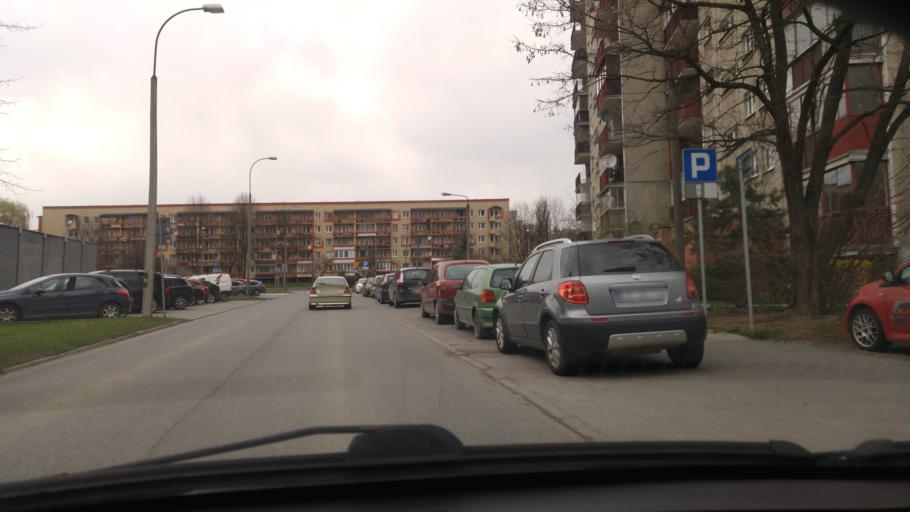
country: PL
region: Lesser Poland Voivodeship
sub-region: Powiat krakowski
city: Michalowice
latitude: 50.0958
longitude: 20.0179
